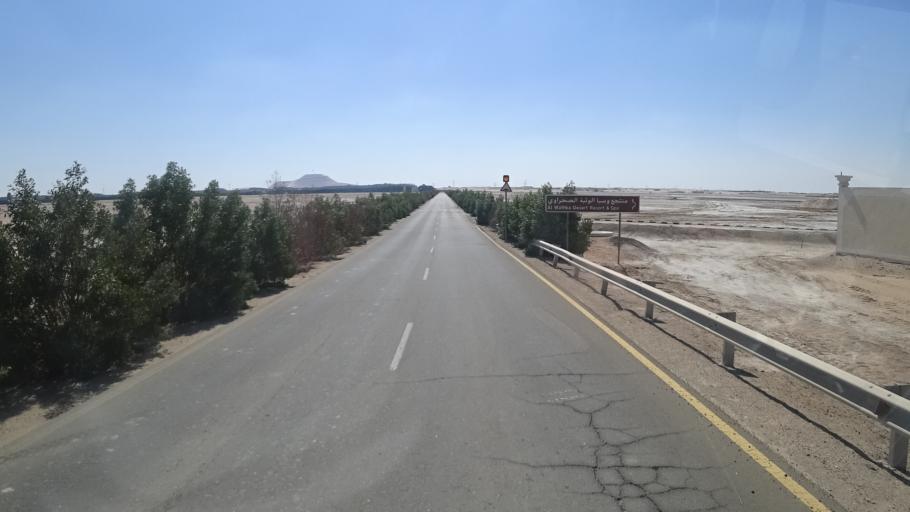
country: AE
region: Abu Dhabi
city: Abu Dhabi
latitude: 24.1978
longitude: 54.7017
